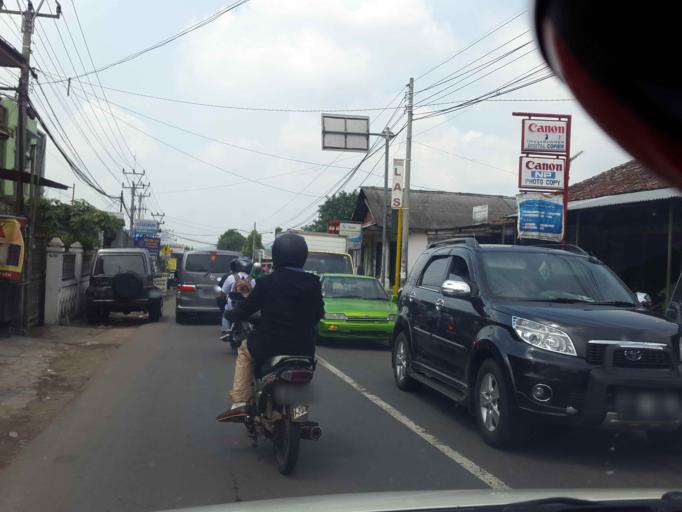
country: ID
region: West Java
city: Sukabumi
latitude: -6.9559
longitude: 106.9091
